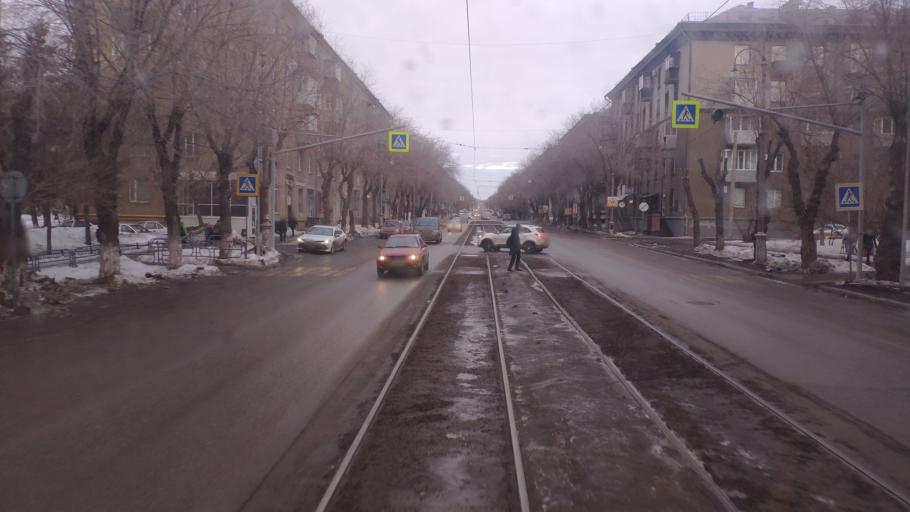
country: RU
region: Chelyabinsk
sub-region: Gorod Magnitogorsk
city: Magnitogorsk
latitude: 53.4178
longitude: 58.9909
